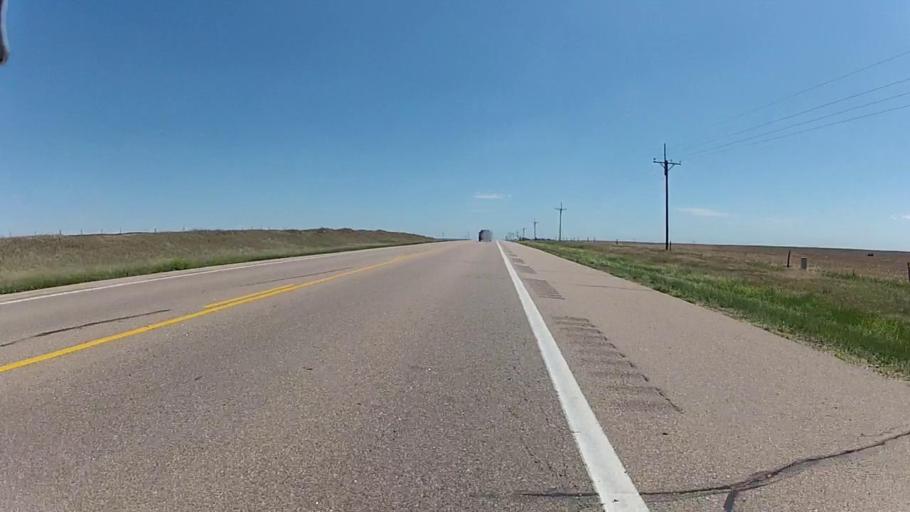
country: US
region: Kansas
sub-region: Ford County
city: Dodge City
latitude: 37.7010
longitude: -100.1481
